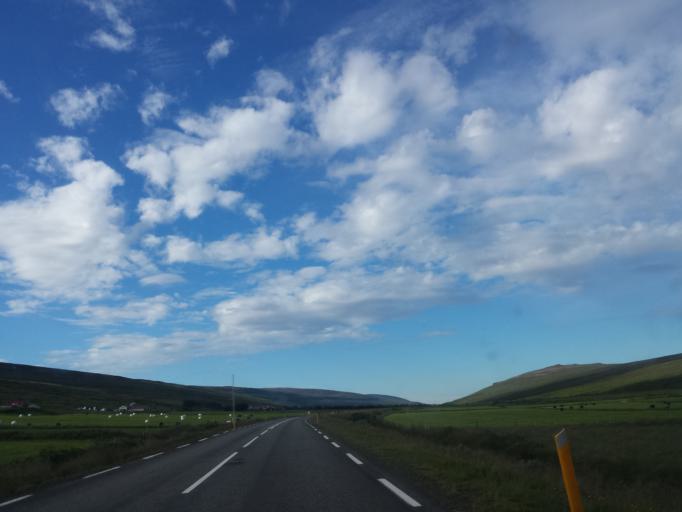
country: IS
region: Northeast
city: Laugar
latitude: 65.7413
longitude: -17.5916
